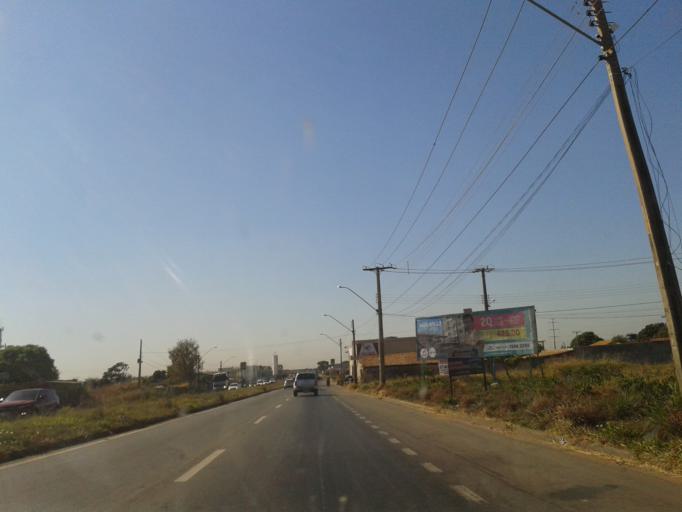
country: BR
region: Goias
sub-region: Aparecida De Goiania
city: Aparecida de Goiania
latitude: -16.7713
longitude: -49.3119
